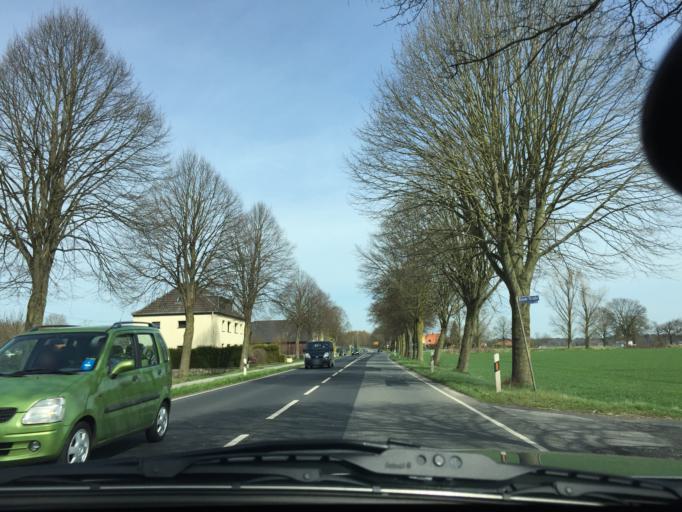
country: DE
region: North Rhine-Westphalia
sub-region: Regierungsbezirk Dusseldorf
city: Goch
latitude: 51.7140
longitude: 6.1580
